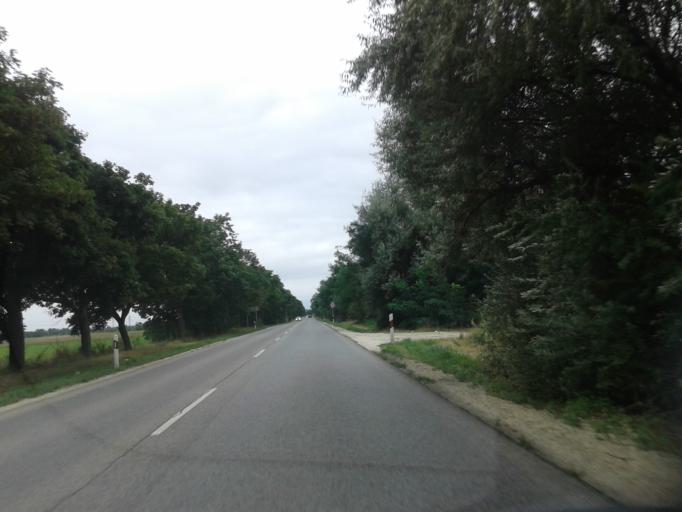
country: HU
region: Pest
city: Dunavarsany
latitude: 47.2848
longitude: 19.0296
